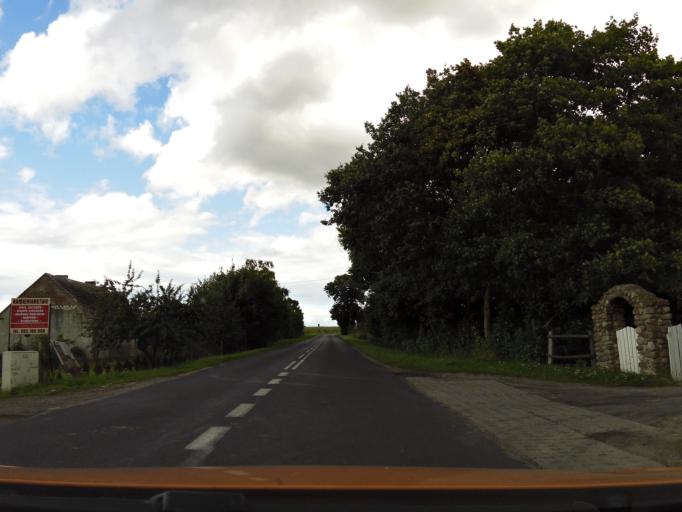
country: PL
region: West Pomeranian Voivodeship
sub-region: Powiat kolobrzeski
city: Goscino
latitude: 54.0780
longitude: 15.5626
